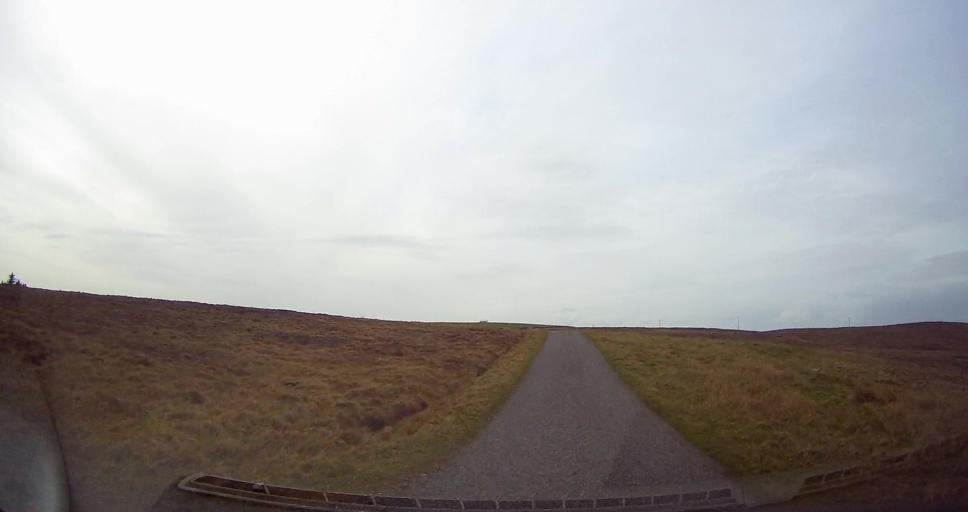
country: GB
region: Scotland
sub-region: Shetland Islands
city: Shetland
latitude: 60.1525
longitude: -1.0912
